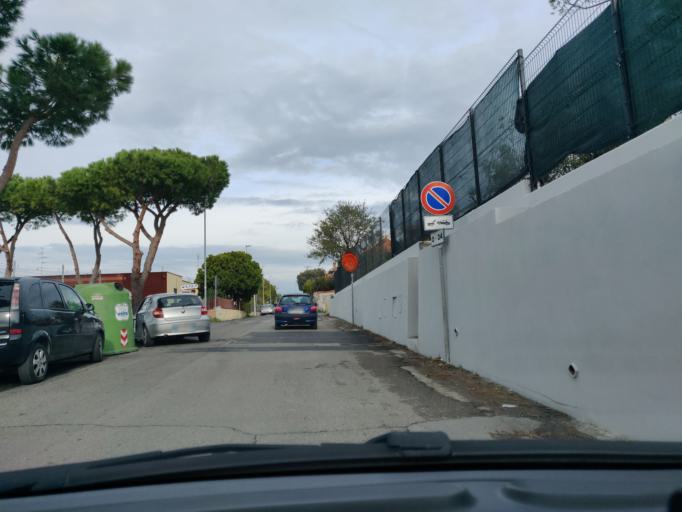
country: IT
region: Latium
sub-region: Citta metropolitana di Roma Capitale
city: Civitavecchia
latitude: 42.0975
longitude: 11.8144
